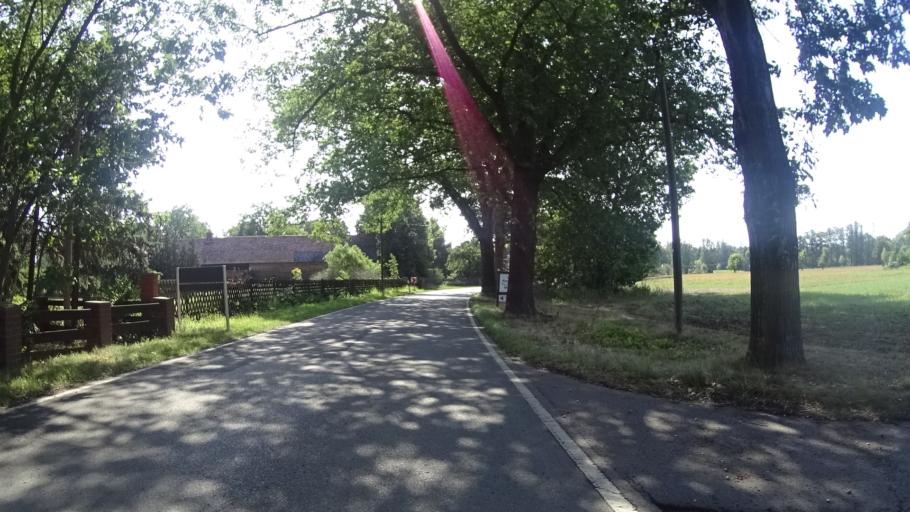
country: DE
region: Brandenburg
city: Burg
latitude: 51.8483
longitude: 14.1386
